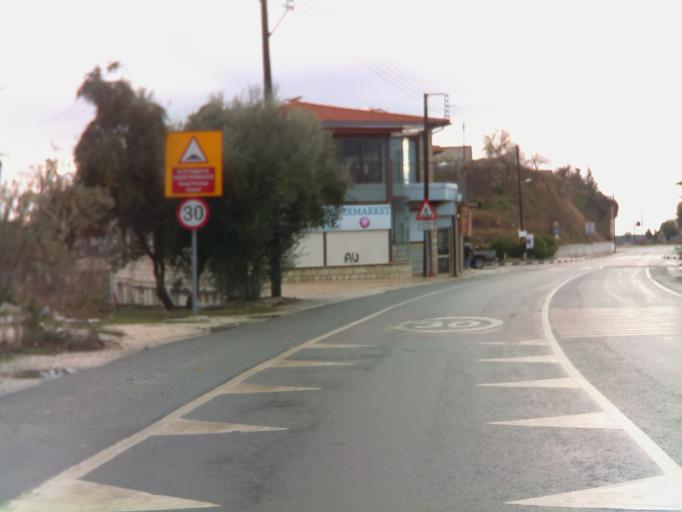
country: CY
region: Pafos
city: Tala
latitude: 34.8910
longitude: 32.4771
